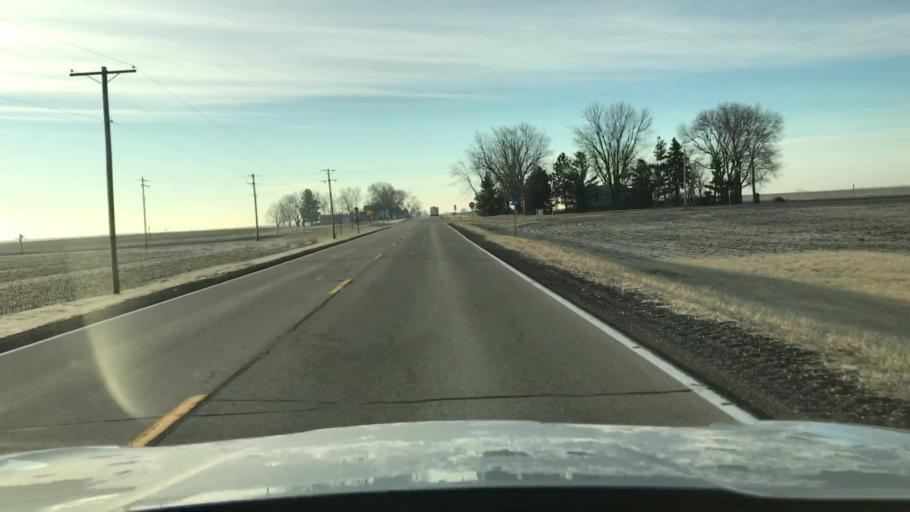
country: US
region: Illinois
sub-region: McLean County
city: Hudson
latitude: 40.6070
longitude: -88.9452
